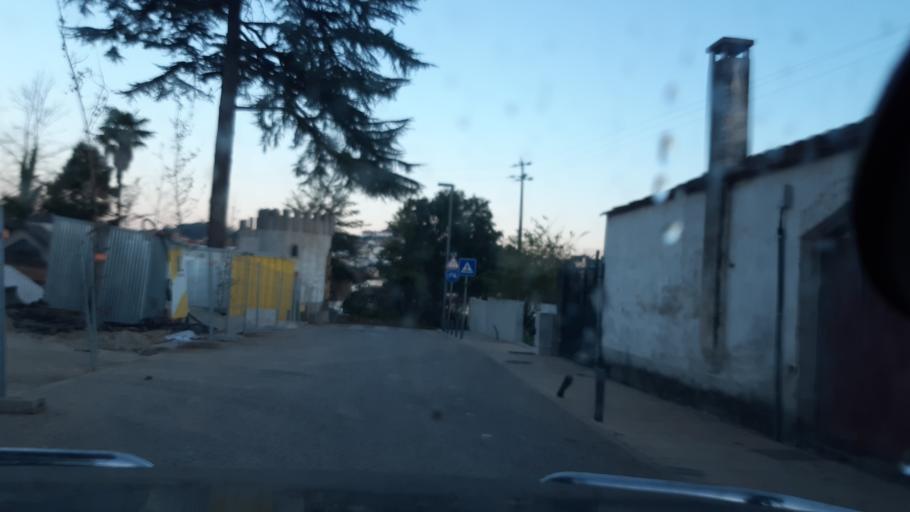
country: PT
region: Aveiro
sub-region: Agueda
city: Agueda
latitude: 40.5743
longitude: -8.4508
